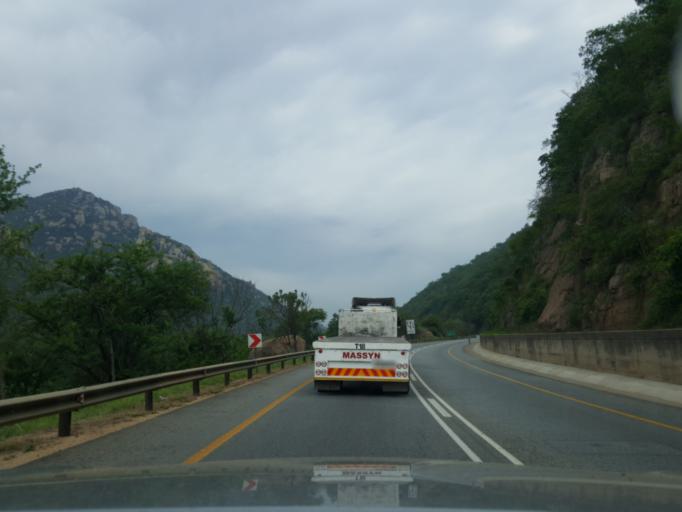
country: ZA
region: Mpumalanga
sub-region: Ehlanzeni District
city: Nelspruit
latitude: -25.5201
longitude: 31.2455
